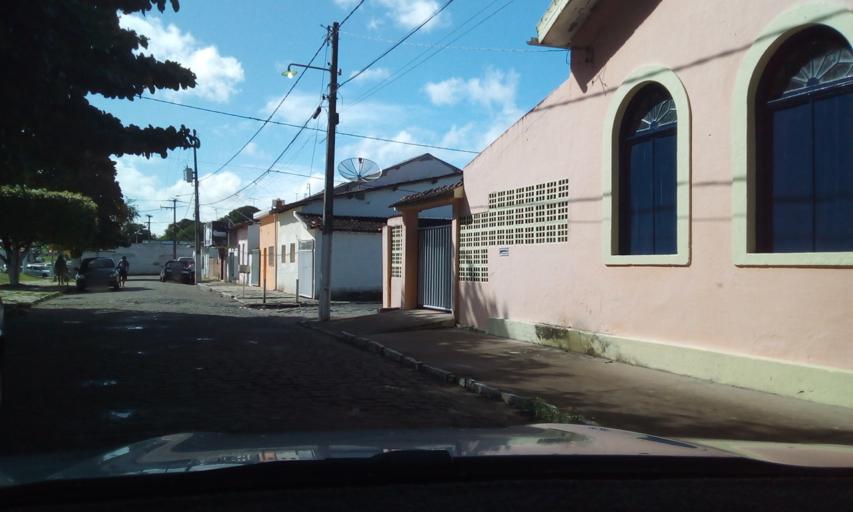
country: BR
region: Paraiba
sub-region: Santa Rita
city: Santa Rita
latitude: -7.1240
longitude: -34.9748
